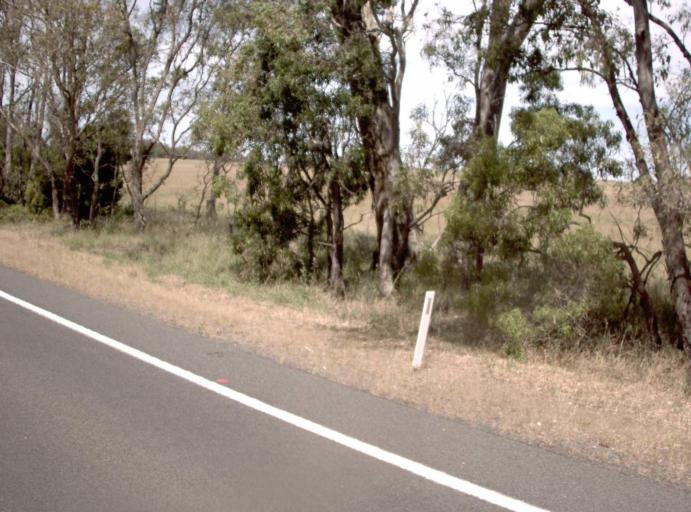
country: AU
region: Victoria
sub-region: Wellington
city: Sale
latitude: -37.9481
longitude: 147.1178
